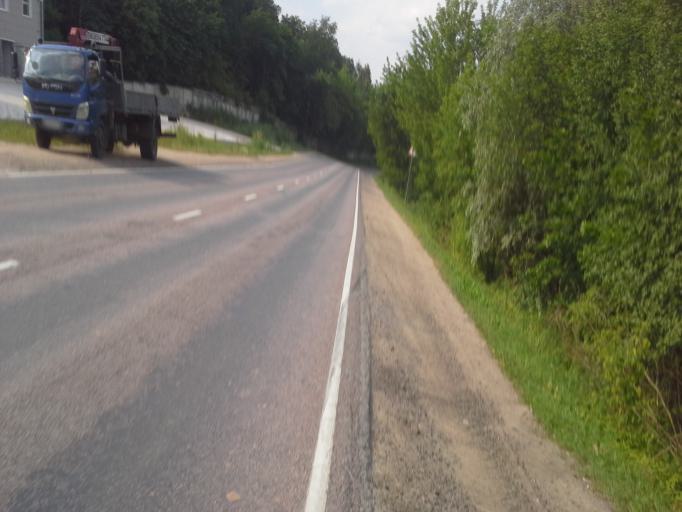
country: RU
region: Moskovskaya
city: Istra
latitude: 55.9015
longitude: 36.8083
